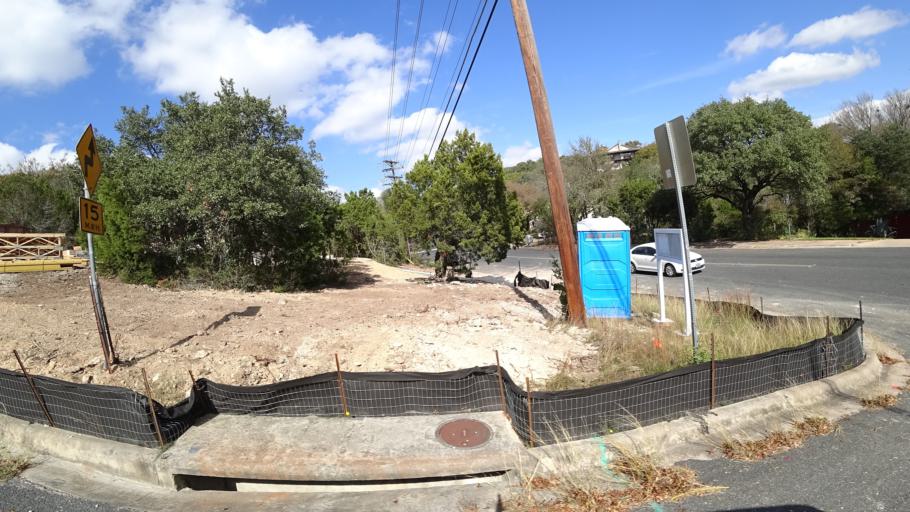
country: US
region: Texas
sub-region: Williamson County
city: Anderson Mill
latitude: 30.4207
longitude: -97.8017
